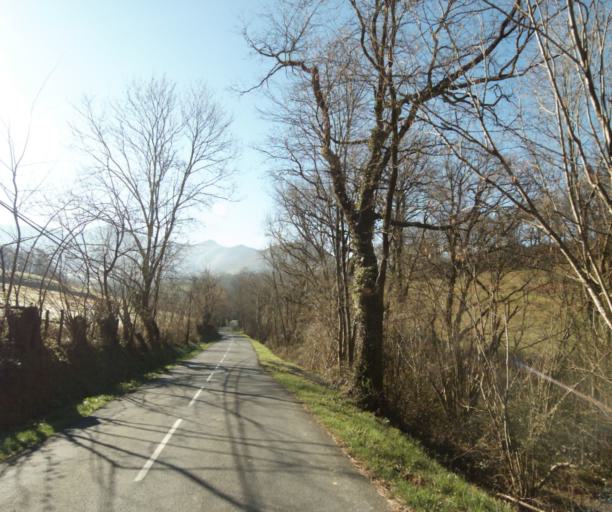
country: FR
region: Aquitaine
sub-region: Departement des Pyrenees-Atlantiques
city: Urrugne
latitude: 43.3429
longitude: -1.6674
